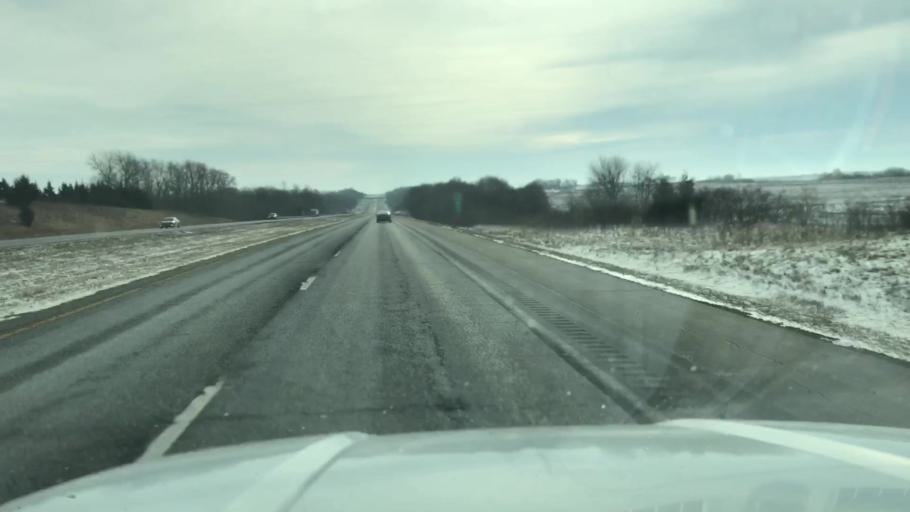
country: US
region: Missouri
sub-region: Holt County
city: Oregon
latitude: 40.0012
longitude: -95.0628
